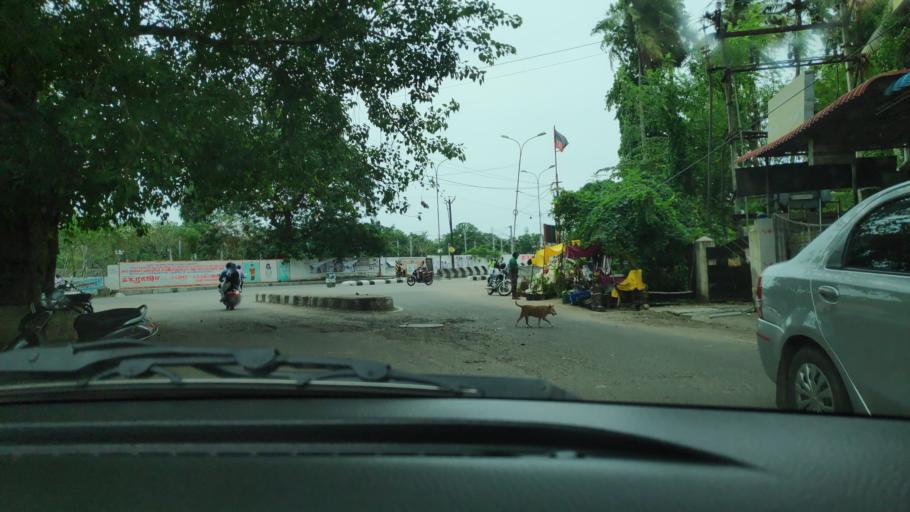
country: IN
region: Tamil Nadu
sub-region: Kancheepuram
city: Pallavaram
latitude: 12.9337
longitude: 80.1297
